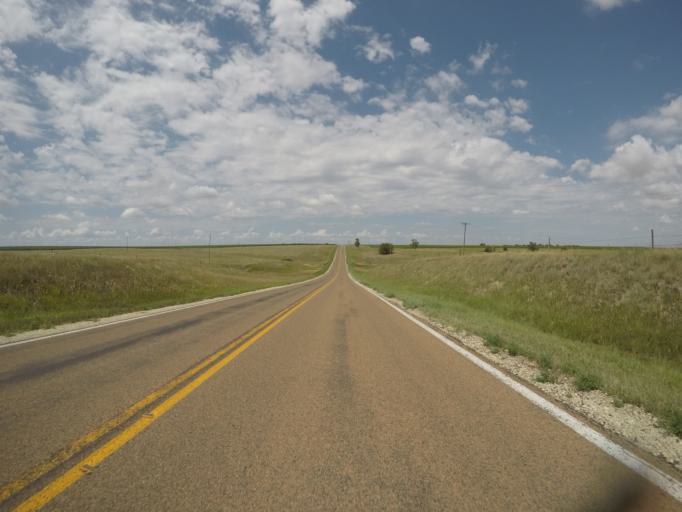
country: US
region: Kansas
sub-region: Rawlins County
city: Atwood
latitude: 39.9666
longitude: -101.0562
